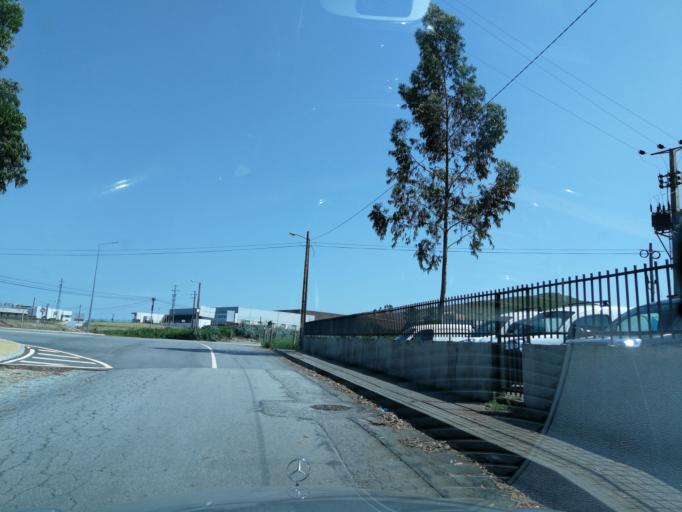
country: PT
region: Braga
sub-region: Braga
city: Adaufe
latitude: 41.5589
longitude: -8.3496
